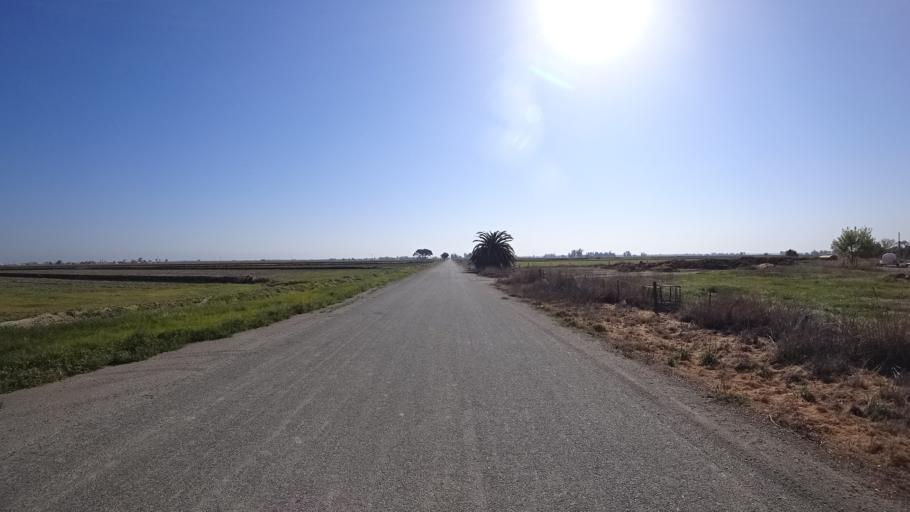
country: US
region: California
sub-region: Glenn County
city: Willows
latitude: 39.6017
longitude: -122.0804
